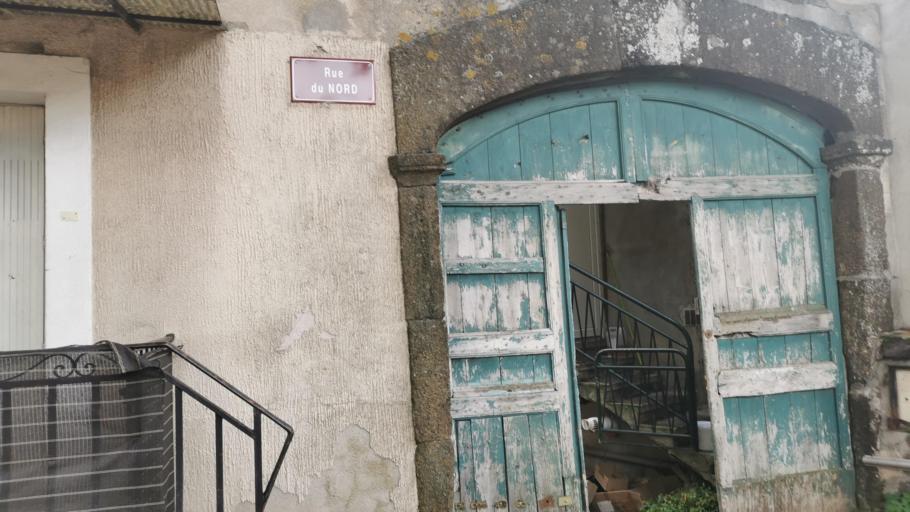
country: FR
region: Auvergne
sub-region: Departement de la Haute-Loire
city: Polignac
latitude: 45.0711
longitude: 3.8604
